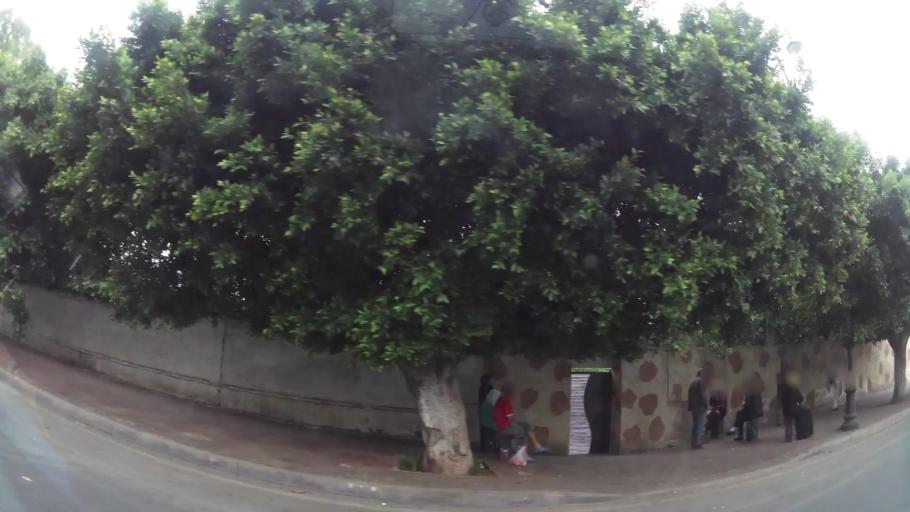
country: MA
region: Rabat-Sale-Zemmour-Zaer
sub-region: Rabat
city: Rabat
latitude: 33.9992
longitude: -6.8611
